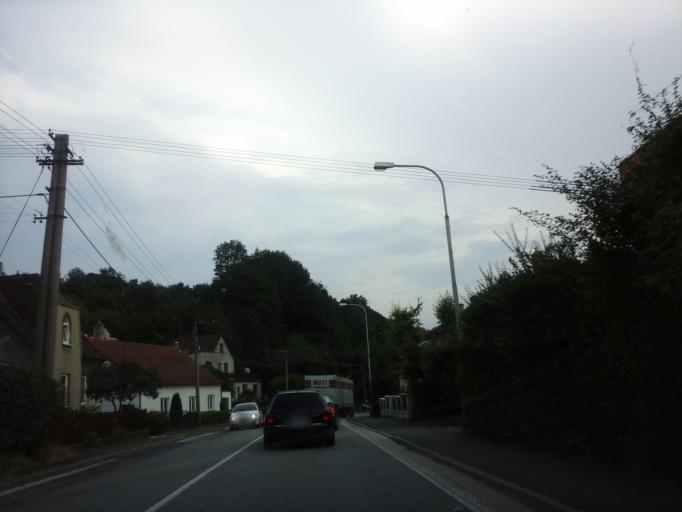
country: CZ
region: Pardubicky
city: Brnenec
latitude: 49.6185
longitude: 16.5309
